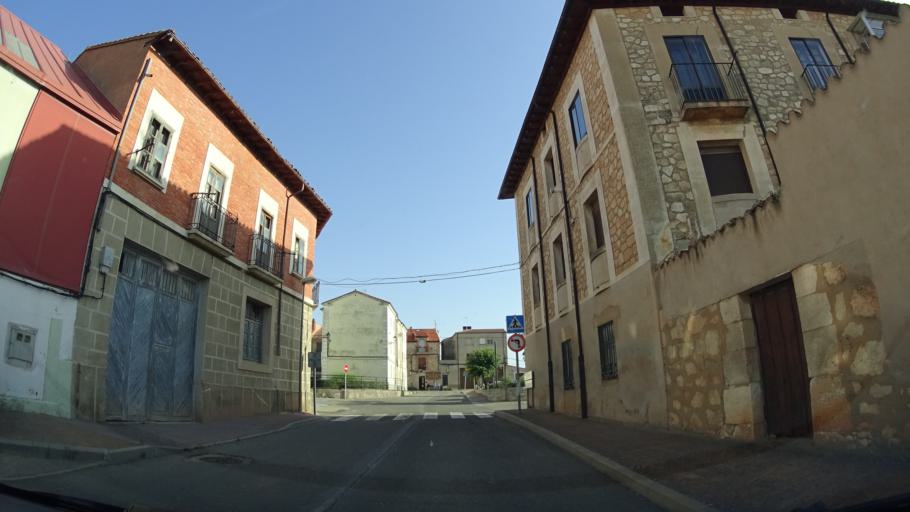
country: ES
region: Castille and Leon
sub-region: Provincia de Burgos
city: Lerma
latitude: 42.0250
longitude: -3.7537
